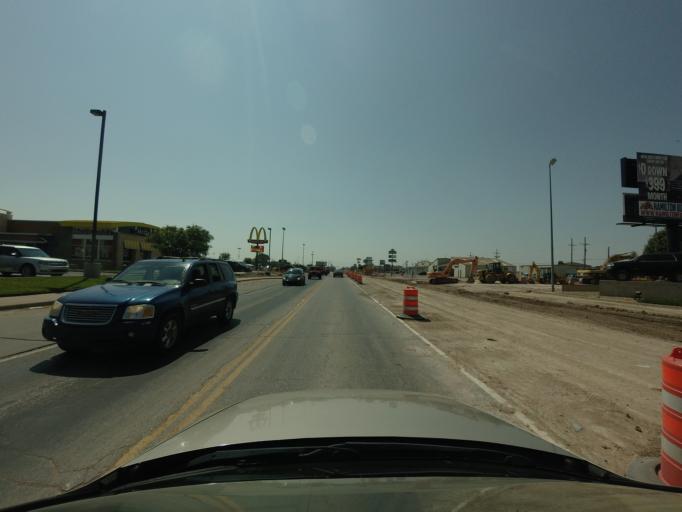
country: US
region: New Mexico
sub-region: Curry County
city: Clovis
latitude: 34.4368
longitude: -103.1964
